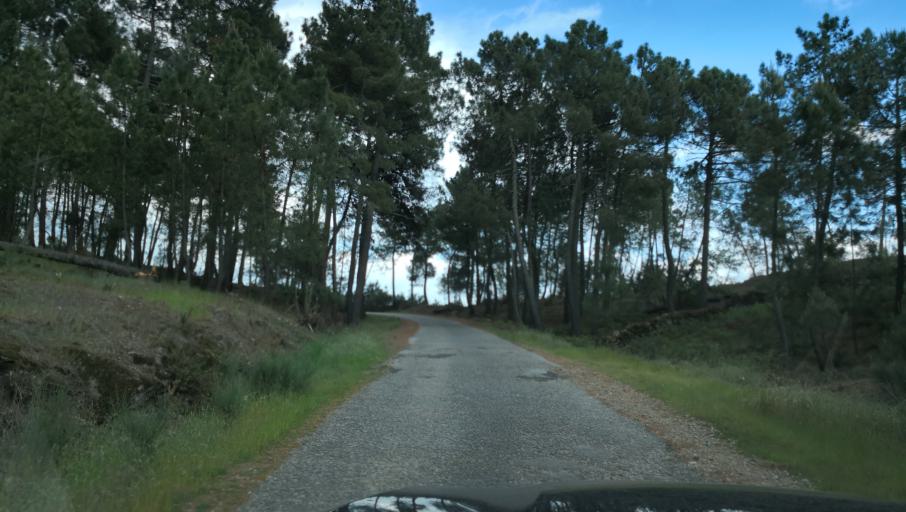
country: PT
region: Vila Real
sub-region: Vila Real
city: Vila Real
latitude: 41.2966
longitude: -7.6920
